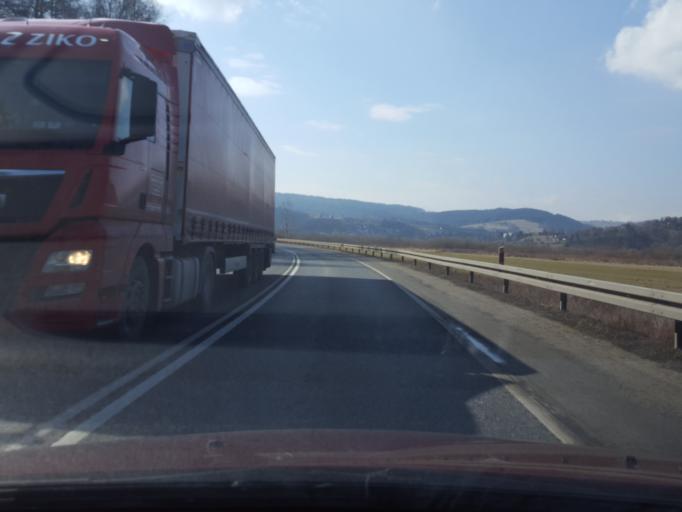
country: PL
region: Lesser Poland Voivodeship
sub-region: Powiat nowosadecki
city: Chelmiec
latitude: 49.6816
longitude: 20.6538
